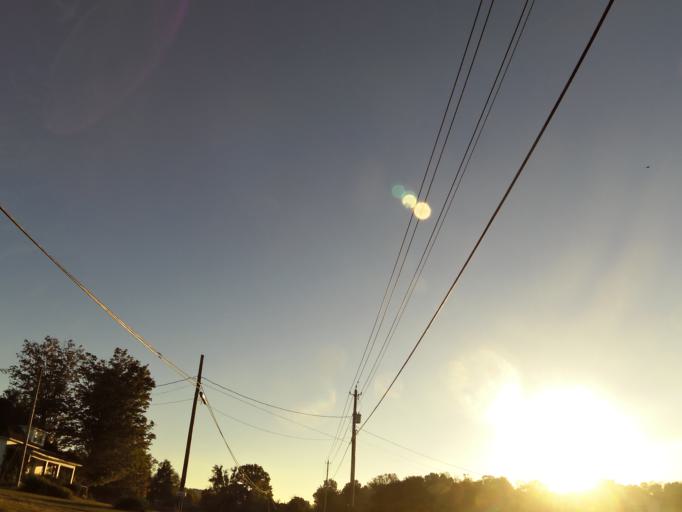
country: US
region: Tennessee
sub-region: Anderson County
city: Clinton
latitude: 36.0033
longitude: -84.0648
